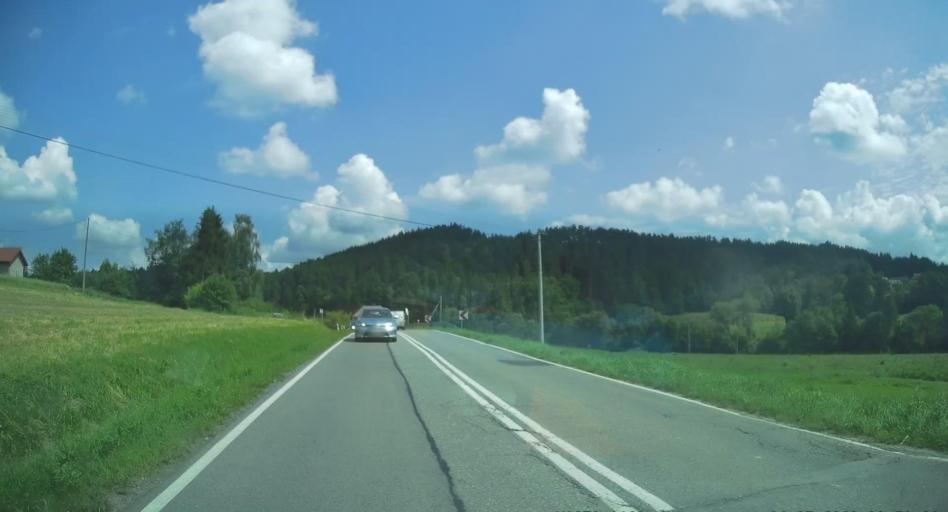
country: PL
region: Lesser Poland Voivodeship
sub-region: Powiat nowosadecki
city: Korzenna
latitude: 49.7555
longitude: 20.7843
